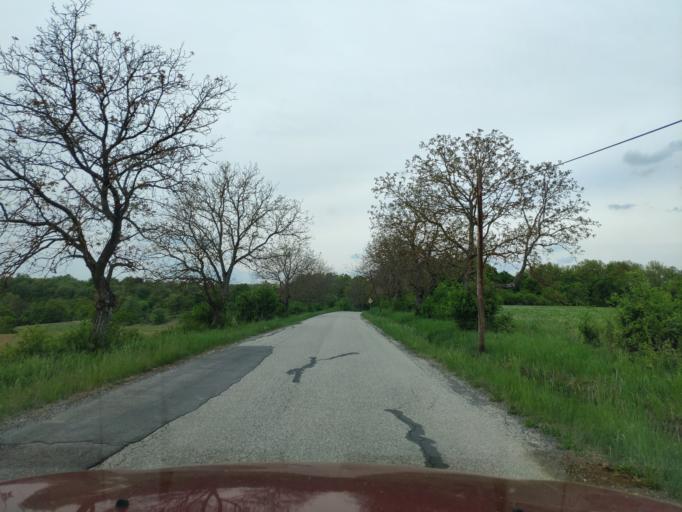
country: SK
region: Banskobystricky
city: Rimavska Sobota
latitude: 48.4927
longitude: 20.0963
